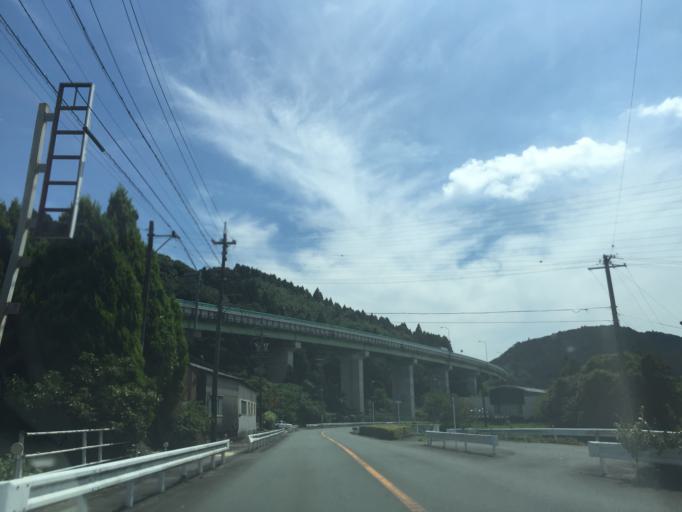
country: JP
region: Shizuoka
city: Kanaya
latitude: 34.8071
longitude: 138.0790
